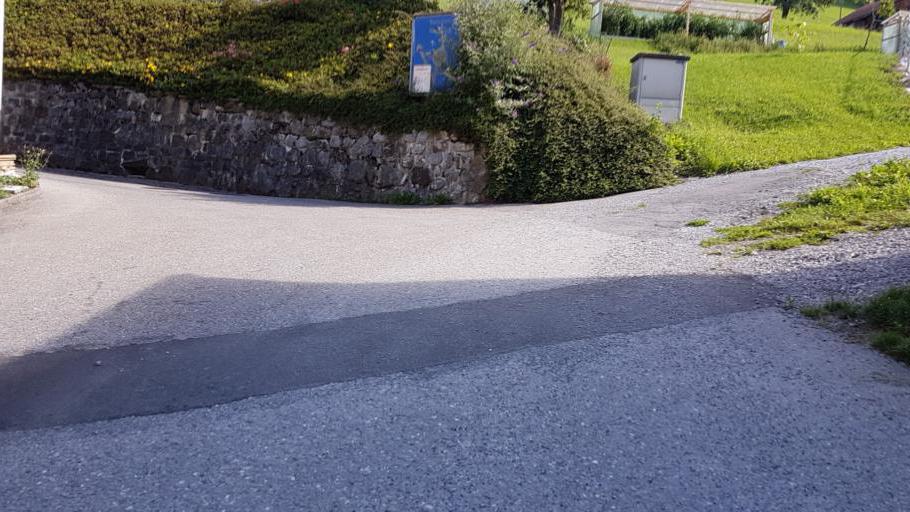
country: CH
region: Bern
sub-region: Obersimmental-Saanen District
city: Boltigen
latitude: 46.6613
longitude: 7.4594
